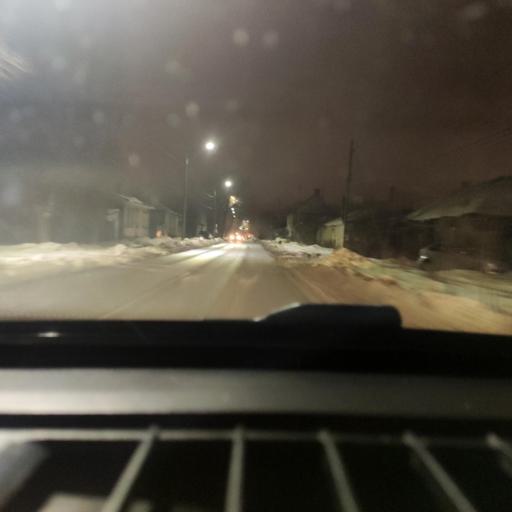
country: RU
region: Voronezj
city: Somovo
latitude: 51.7383
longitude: 39.2670
